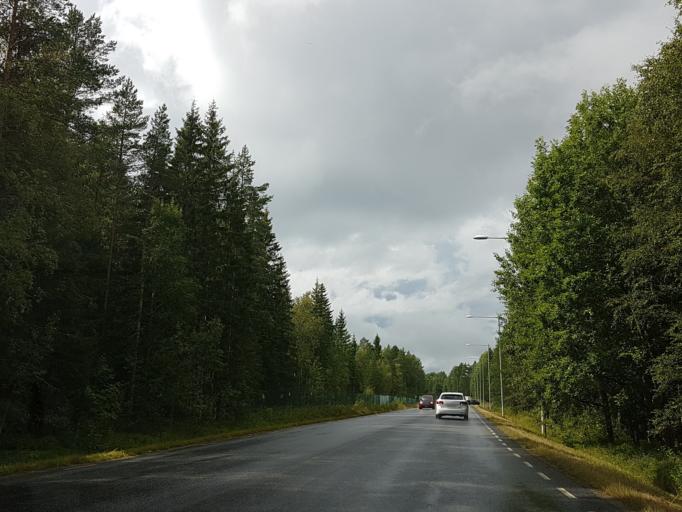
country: SE
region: Vaesterbotten
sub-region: Umea Kommun
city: Ersmark
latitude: 63.8527
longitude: 20.3431
